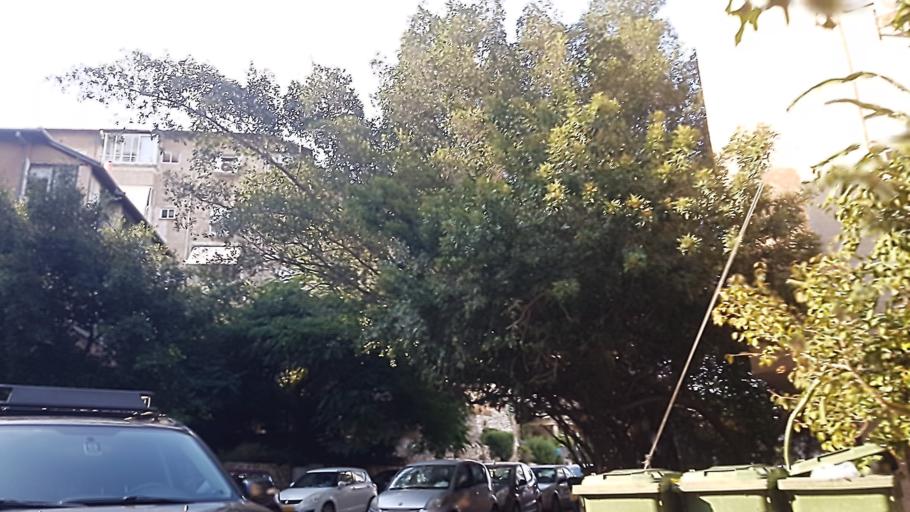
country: IL
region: Tel Aviv
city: Ramat Gan
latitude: 32.0805
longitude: 34.8136
